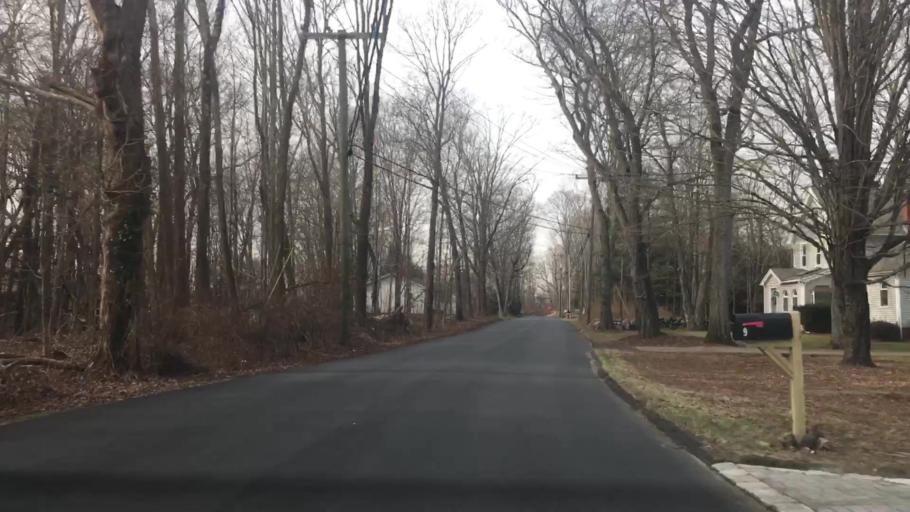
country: US
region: Connecticut
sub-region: Fairfield County
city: Newtown
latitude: 41.3675
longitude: -73.2553
